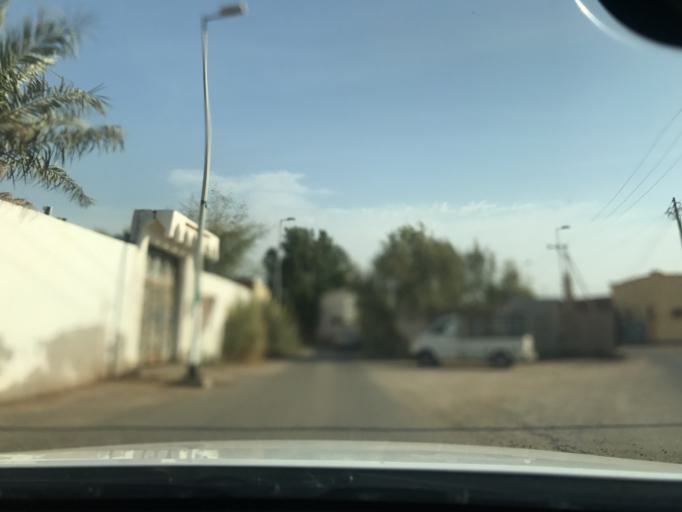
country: SA
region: Makkah
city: Al Jumum
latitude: 21.4485
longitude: 39.5331
